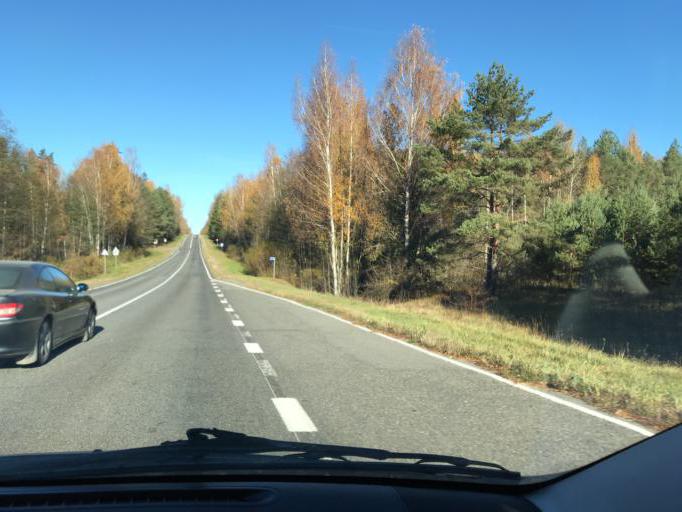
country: BY
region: Vitebsk
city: Lyepyel'
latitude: 54.9788
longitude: 28.7448
